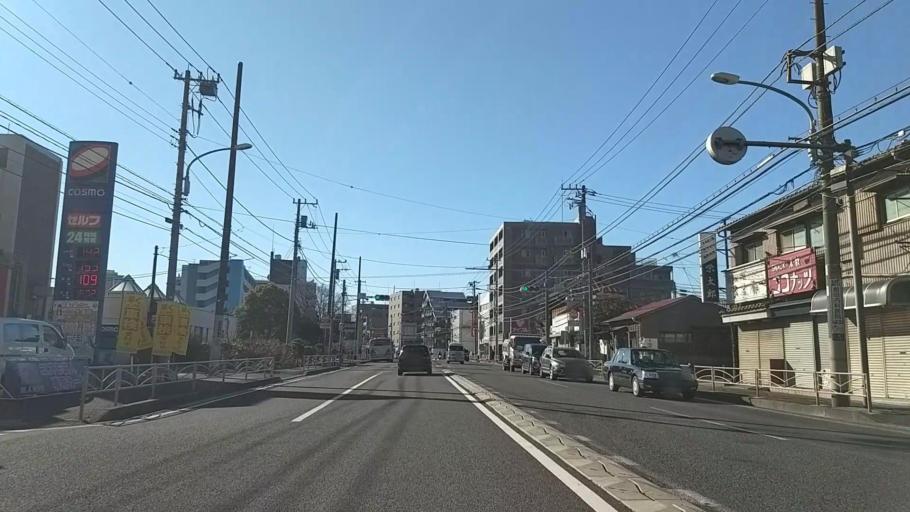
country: JP
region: Kanagawa
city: Yokohama
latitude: 35.3941
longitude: 139.6144
